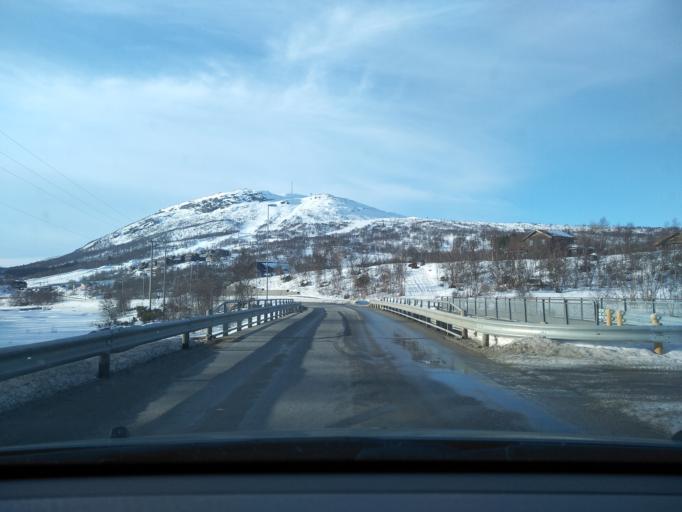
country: NO
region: Aust-Agder
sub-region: Bykle
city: Hovden
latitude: 59.5682
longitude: 7.3597
